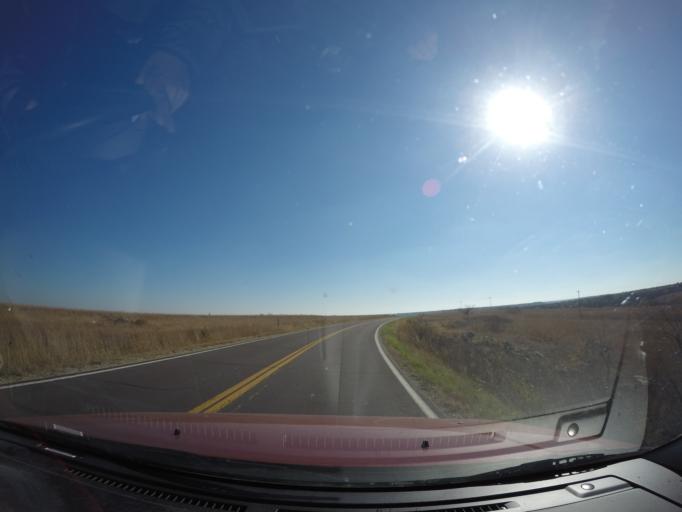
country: US
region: Kansas
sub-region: Geary County
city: Grandview Plaza
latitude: 39.0141
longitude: -96.7546
